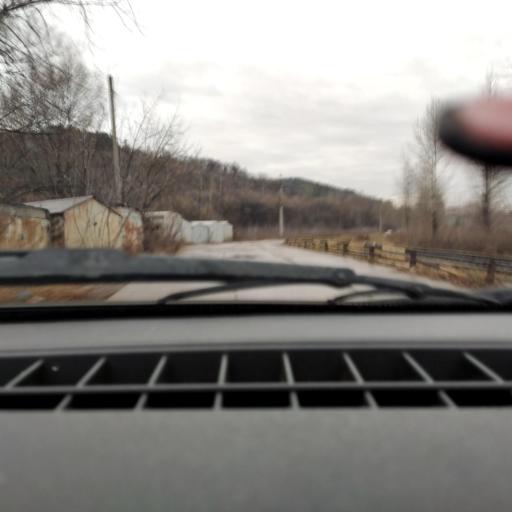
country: RU
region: Bashkortostan
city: Ufa
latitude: 54.7637
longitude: 55.9803
